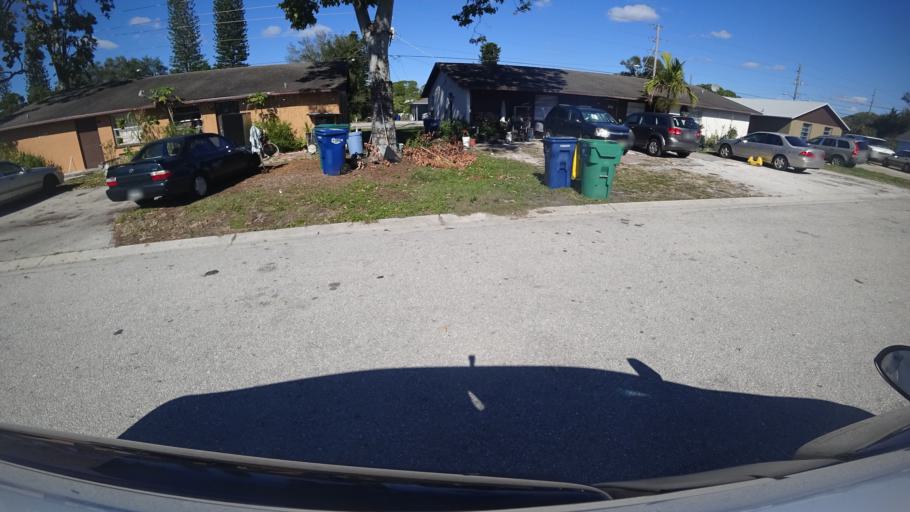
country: US
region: Florida
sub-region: Manatee County
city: West Samoset
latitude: 27.4399
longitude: -82.5535
